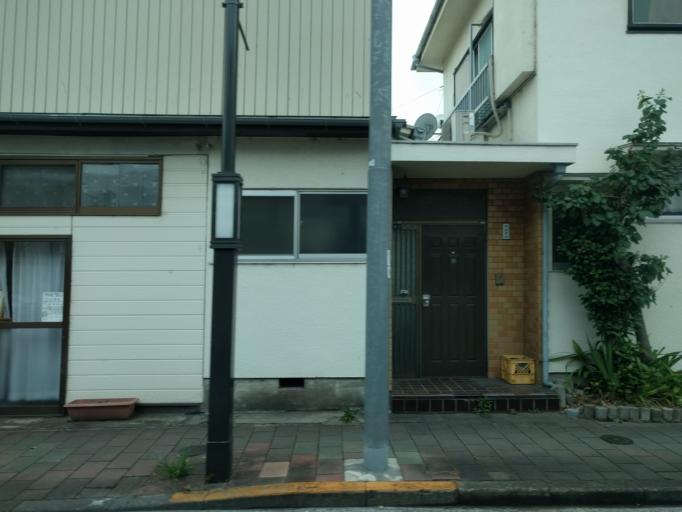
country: JP
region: Kanagawa
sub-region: Kawasaki-shi
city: Kawasaki
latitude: 35.5896
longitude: 139.6737
